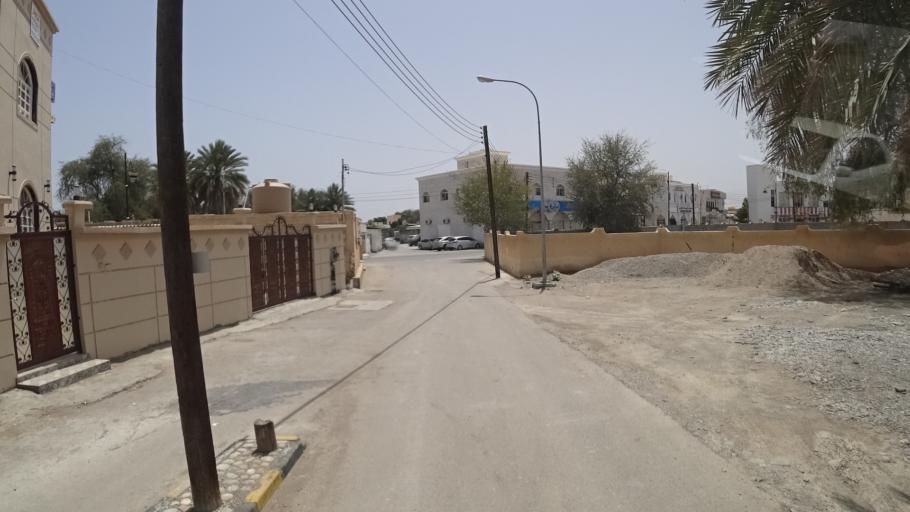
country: OM
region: Muhafazat Masqat
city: Muscat
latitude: 23.2607
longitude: 58.9148
